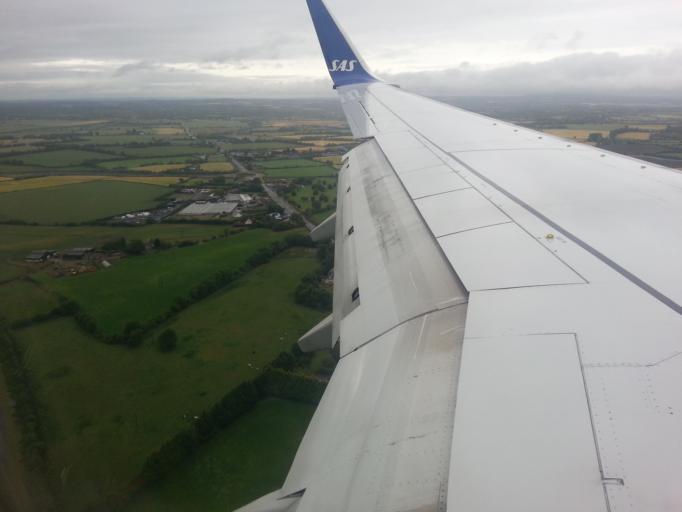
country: IE
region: Leinster
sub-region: Dublin City
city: Finglas
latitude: 53.4255
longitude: -6.3299
